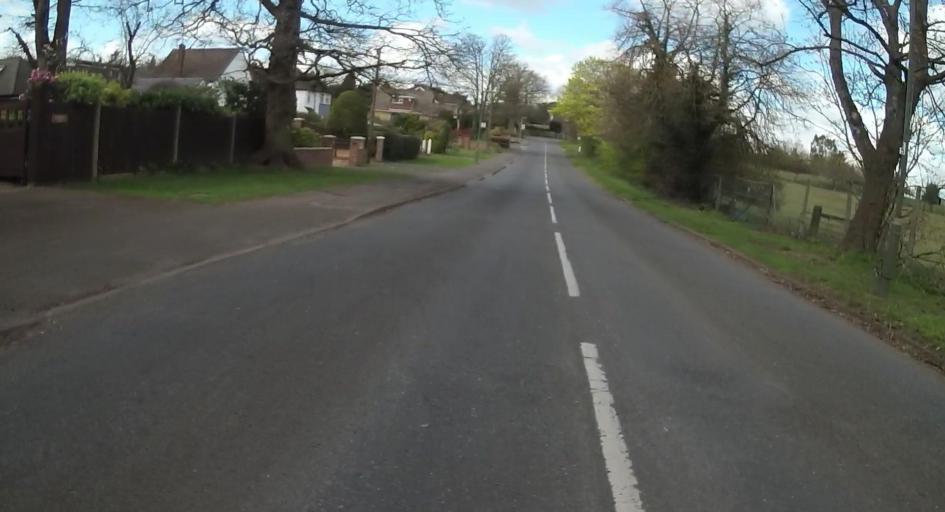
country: GB
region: England
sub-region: Surrey
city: West Byfleet
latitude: 51.3497
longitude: -0.5114
